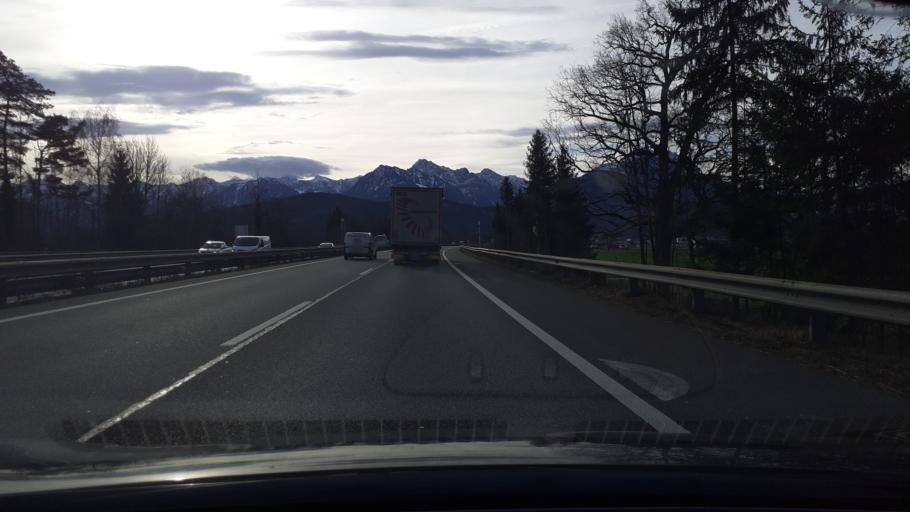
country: AT
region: Vorarlberg
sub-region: Politischer Bezirk Feldkirch
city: Rankweil
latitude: 47.2899
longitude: 9.6262
